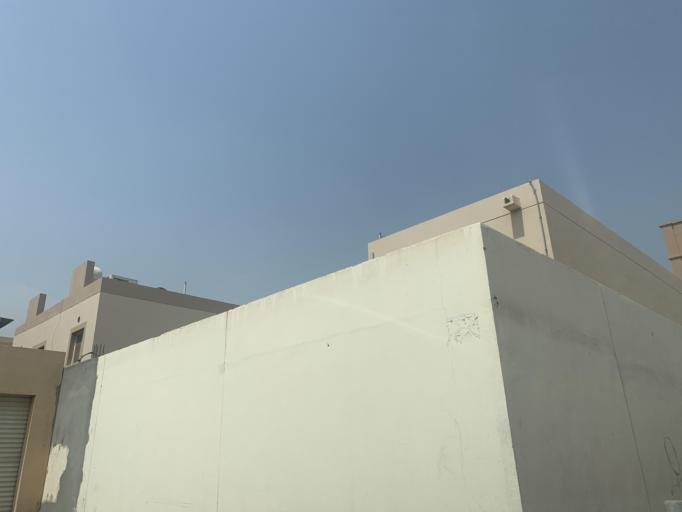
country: BH
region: Manama
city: Jidd Hafs
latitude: 26.2079
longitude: 50.5082
